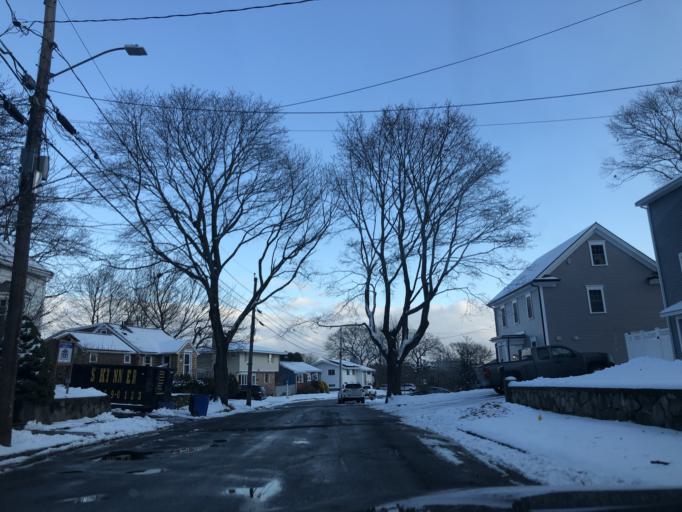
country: US
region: Massachusetts
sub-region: Middlesex County
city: Arlington
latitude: 42.4270
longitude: -71.1679
